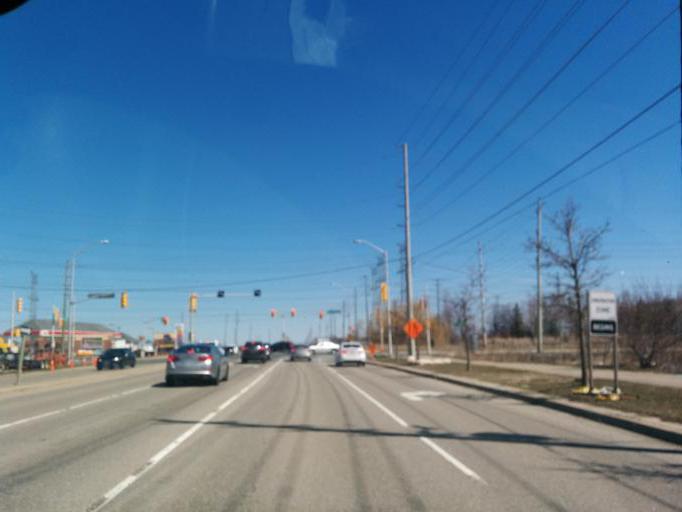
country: CA
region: Ontario
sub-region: Halton
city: Milton
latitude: 43.5372
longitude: -79.8570
